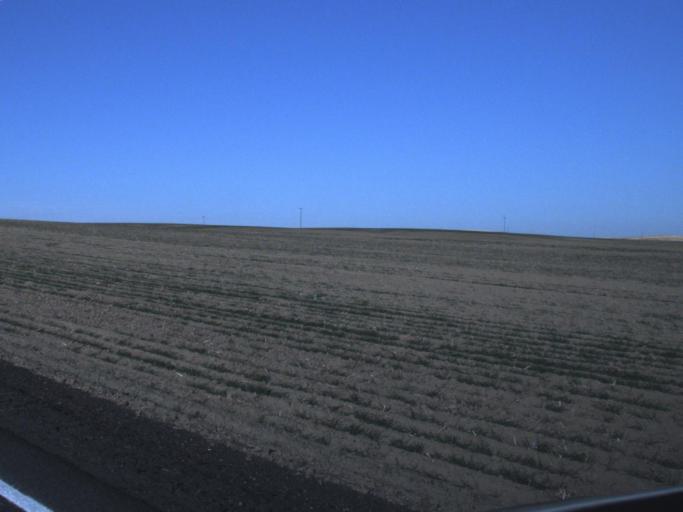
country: US
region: Washington
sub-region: Adams County
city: Ritzville
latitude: 47.0260
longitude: -118.3498
